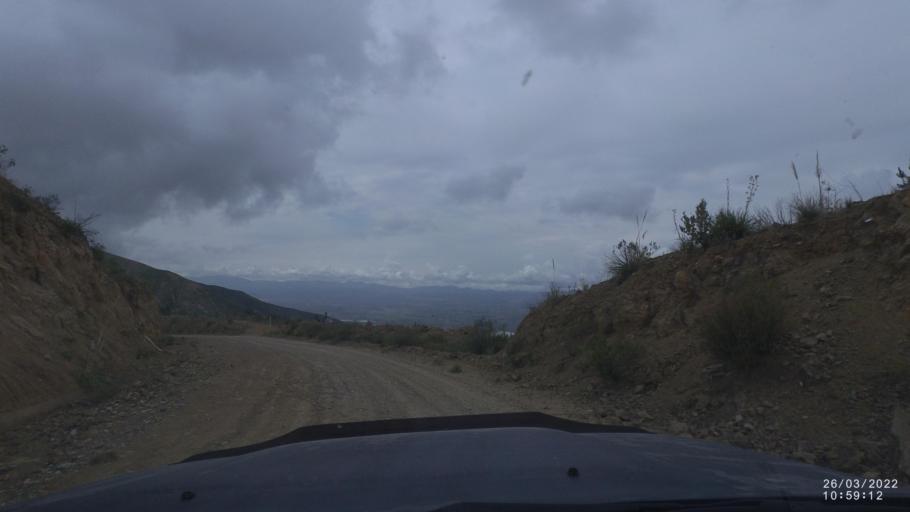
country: BO
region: Cochabamba
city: Tarata
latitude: -17.5135
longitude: -66.0273
